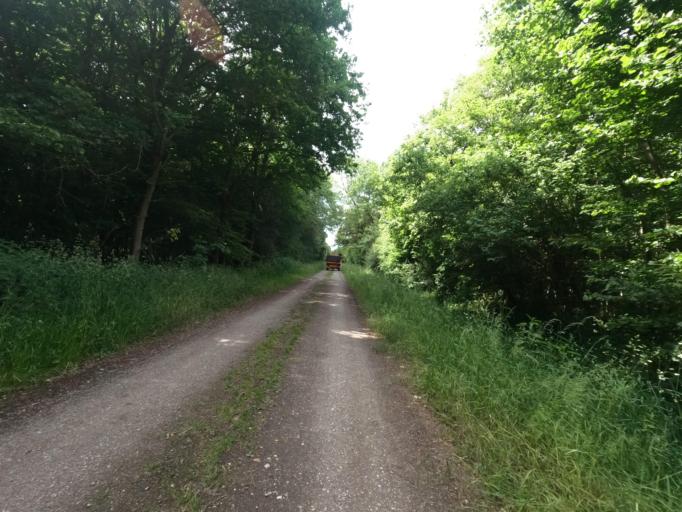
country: DE
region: North Rhine-Westphalia
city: Huckelhoven
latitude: 51.0227
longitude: 6.2158
